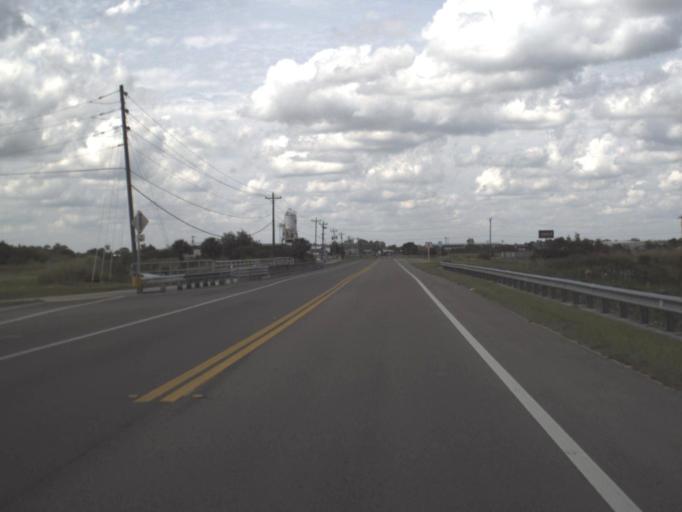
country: US
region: Florida
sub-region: Collier County
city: Immokalee
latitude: 26.4113
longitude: -81.4006
